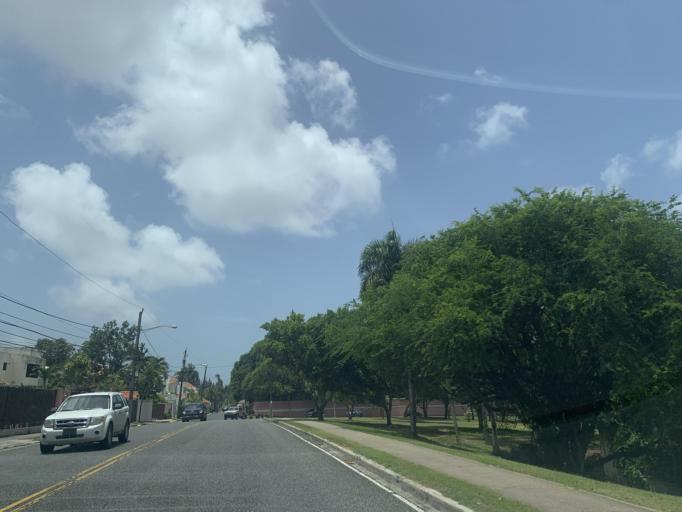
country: DO
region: Nacional
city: La Agustina
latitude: 18.4984
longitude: -69.9482
